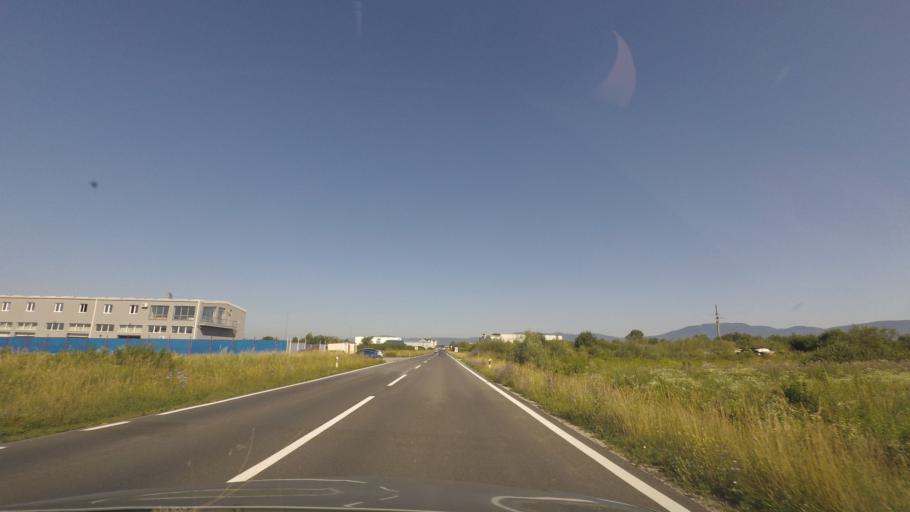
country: HR
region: Zagrebacka
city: Jastrebarsko
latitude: 45.6494
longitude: 15.6660
